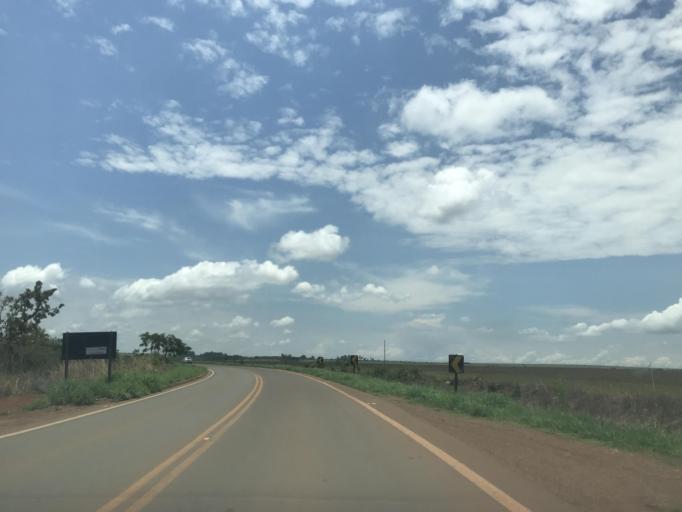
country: BR
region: Goias
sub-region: Luziania
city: Luziania
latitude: -16.4655
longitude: -48.2146
